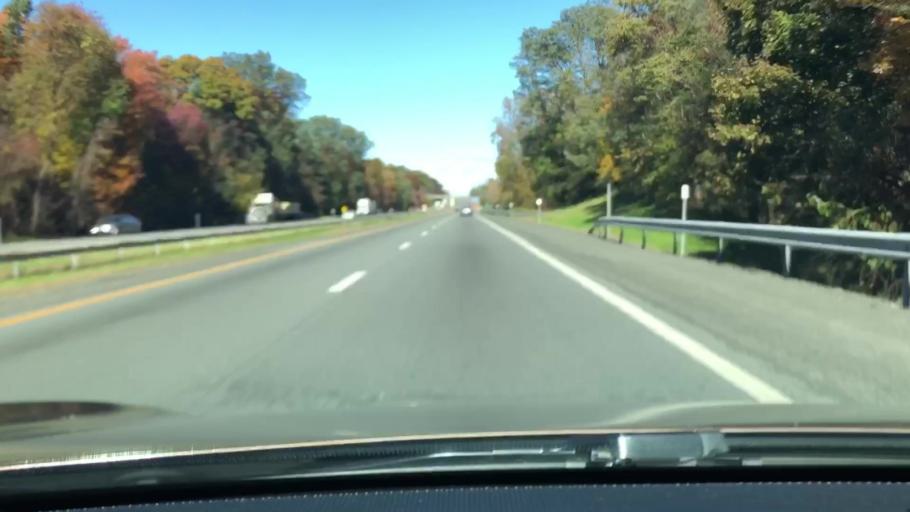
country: US
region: New York
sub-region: Orange County
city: Firthcliffe
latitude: 41.4226
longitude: -74.0687
